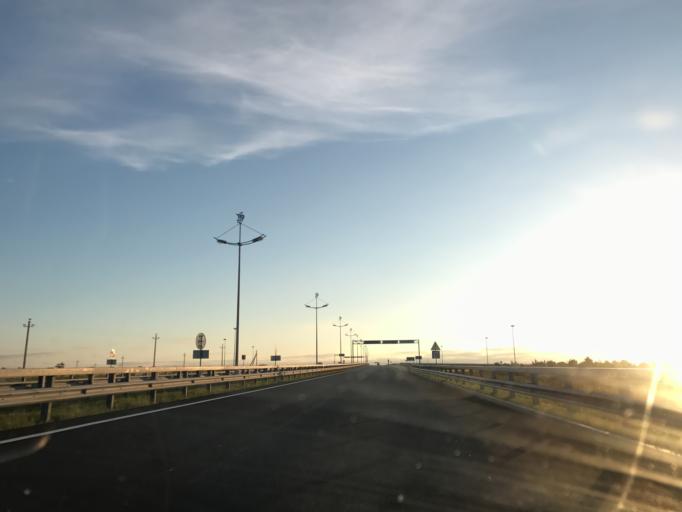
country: RU
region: Kaliningrad
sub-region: Gorod Kaliningrad
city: Pionerskiy
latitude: 54.9213
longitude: 20.3359
